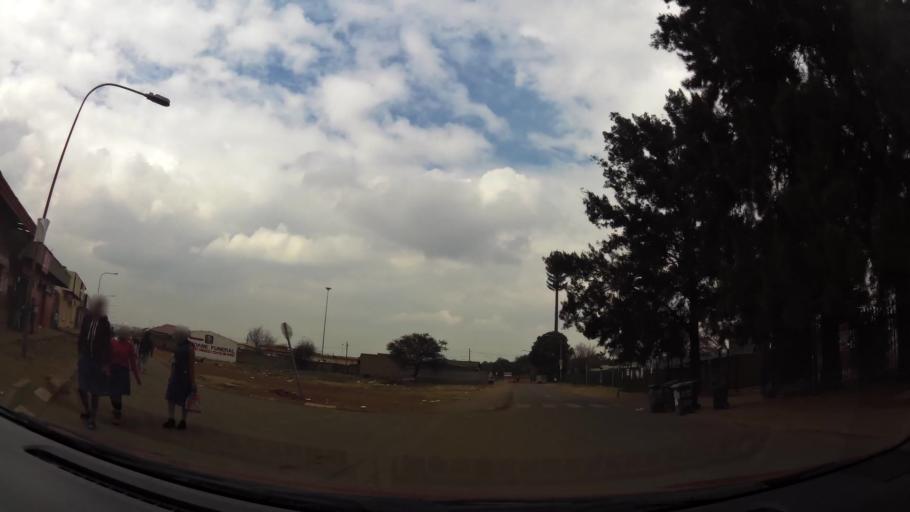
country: ZA
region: Gauteng
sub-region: City of Johannesburg Metropolitan Municipality
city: Soweto
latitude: -26.2588
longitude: 27.8286
